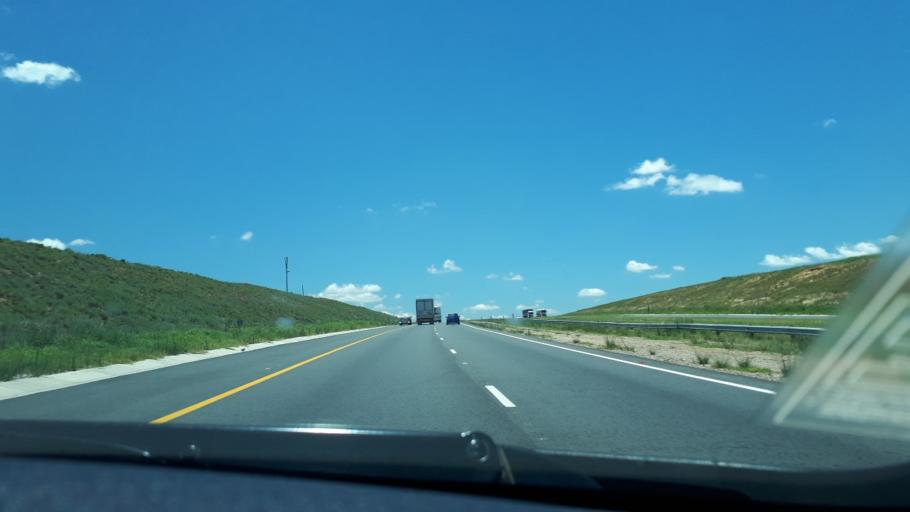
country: ZA
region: Gauteng
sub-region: City of Johannesburg Metropolitan Municipality
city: Diepsloot
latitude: -25.9414
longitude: 27.9651
